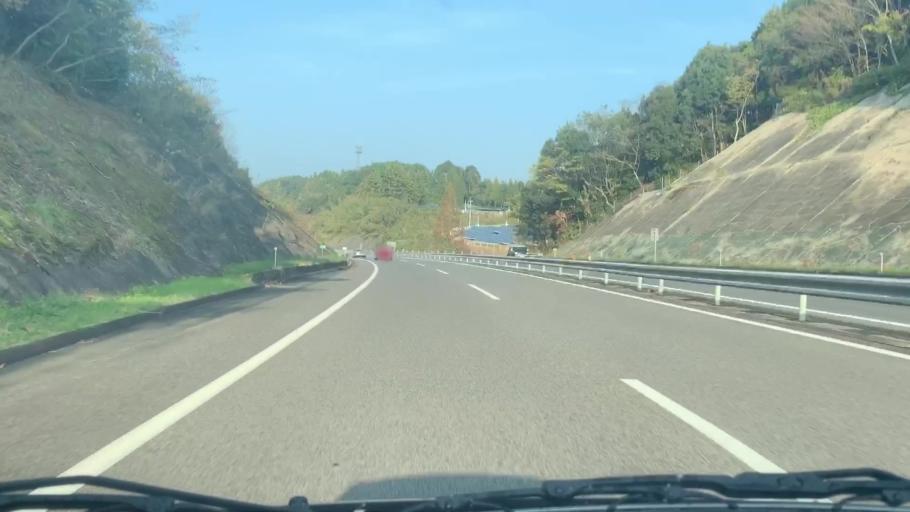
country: JP
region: Saga Prefecture
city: Ureshinomachi-shimojuku
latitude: 33.1532
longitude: 129.9334
